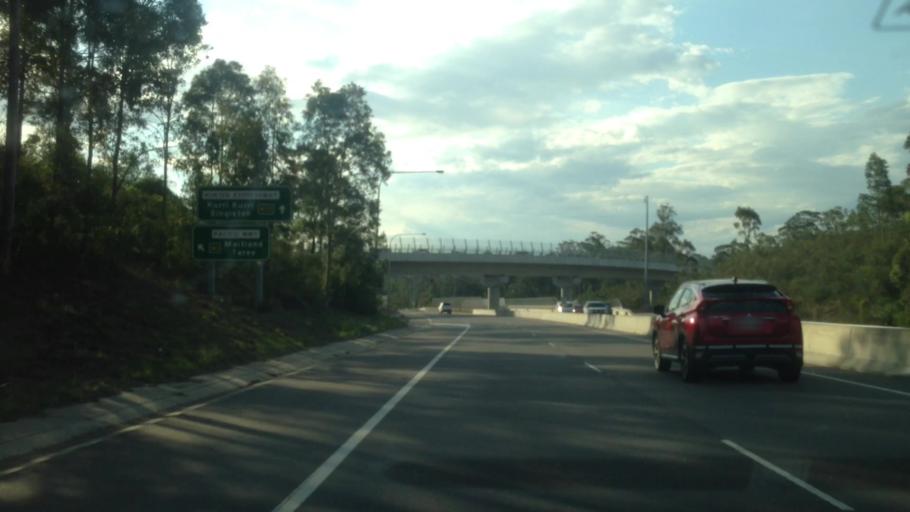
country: AU
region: New South Wales
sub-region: Lake Macquarie Shire
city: Holmesville
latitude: -32.8905
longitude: 151.6027
